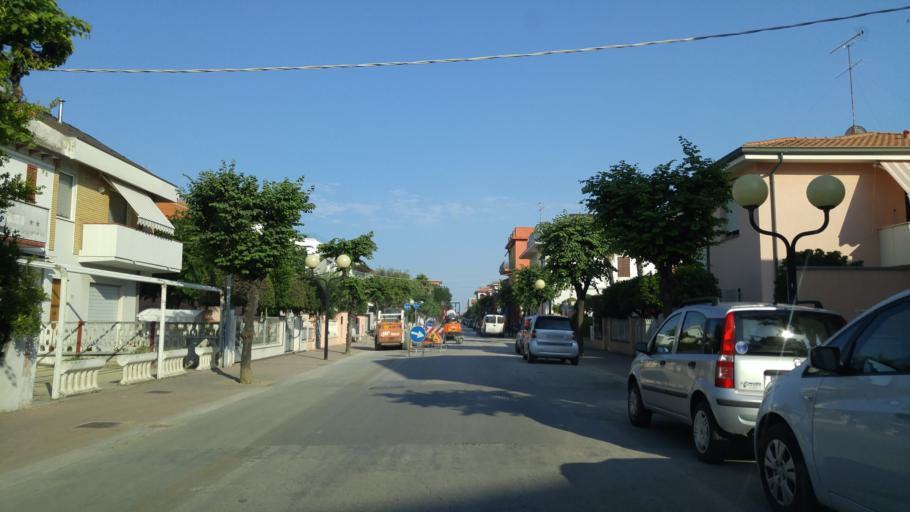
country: IT
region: The Marches
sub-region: Provincia di Pesaro e Urbino
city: Marotta
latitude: 43.7706
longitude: 13.1370
